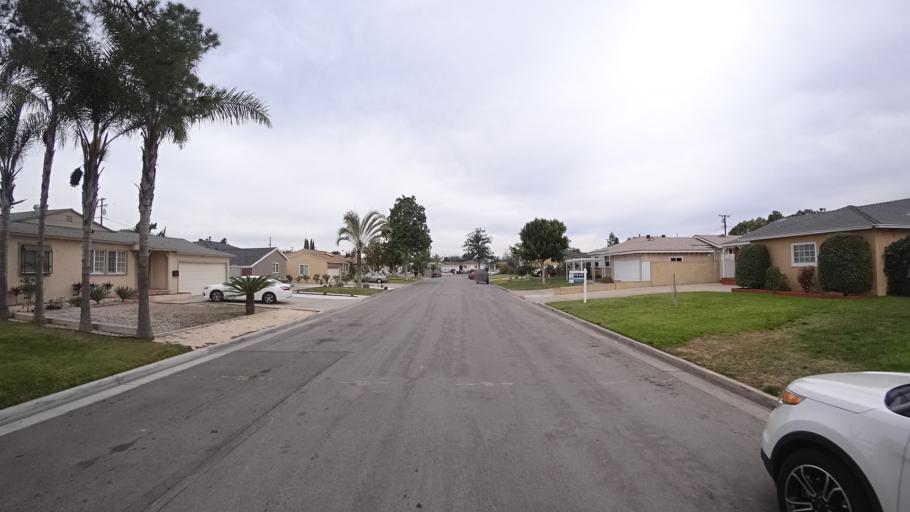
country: US
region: California
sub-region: Orange County
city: Garden Grove
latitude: 33.7791
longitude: -117.9285
